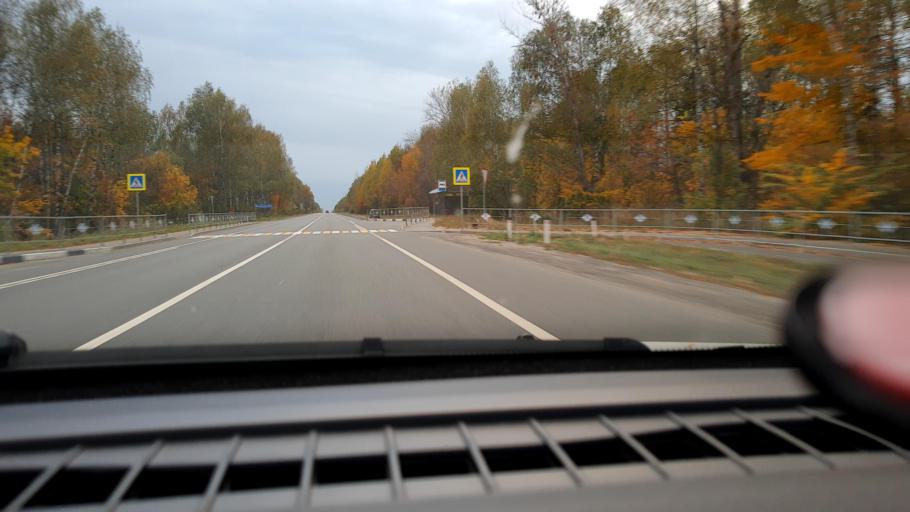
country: RU
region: Vladimir
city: Kameshkovo
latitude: 56.1965
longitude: 40.8766
